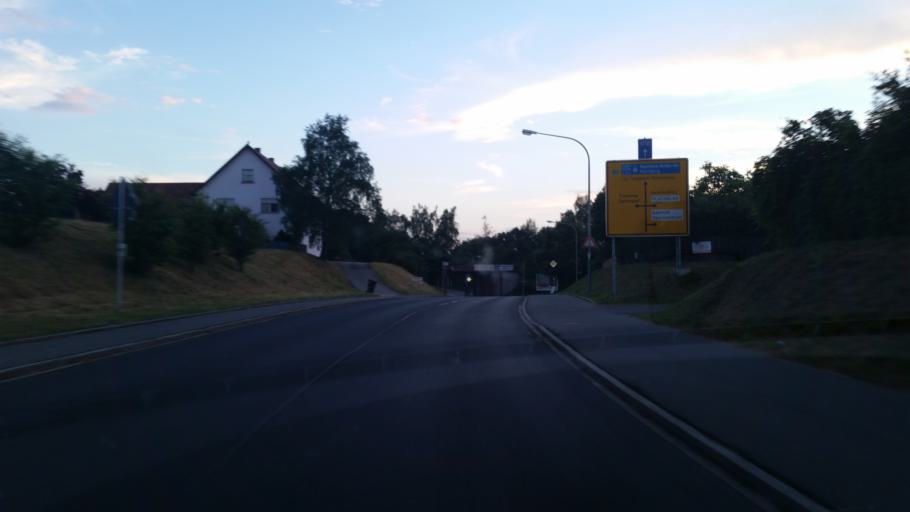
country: DE
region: Bavaria
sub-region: Upper Palatinate
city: Wernberg-Koblitz
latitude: 49.5367
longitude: 12.1514
